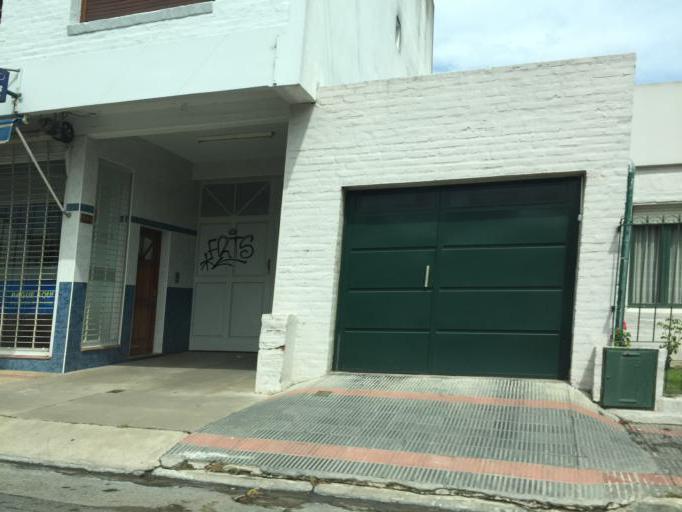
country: AR
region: Buenos Aires
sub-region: Partido de Tandil
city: Tandil
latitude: -37.3259
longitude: -59.1131
